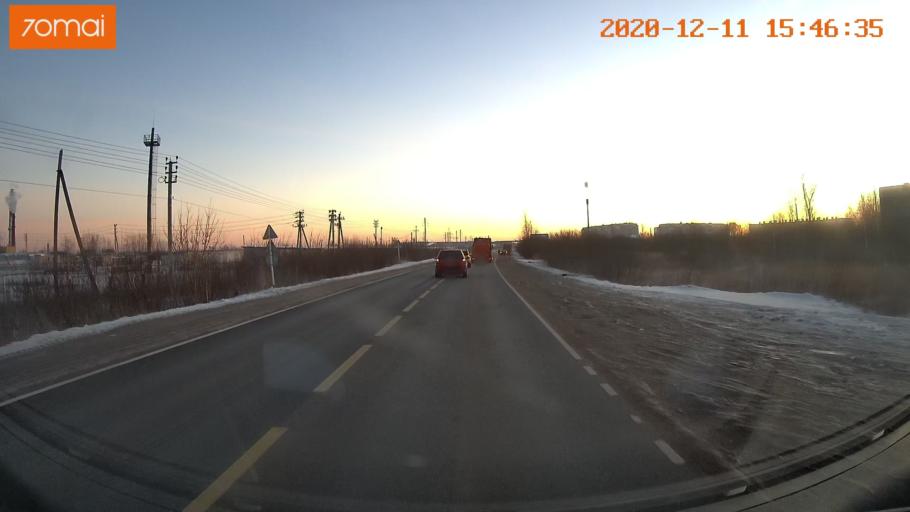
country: RU
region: Ivanovo
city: Novo-Talitsy
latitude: 57.0050
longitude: 40.8549
